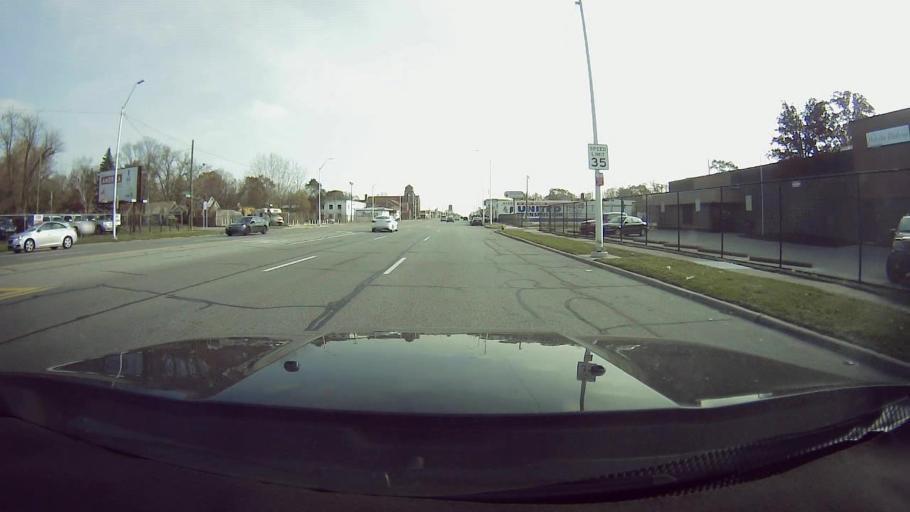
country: US
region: Michigan
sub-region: Wayne County
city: Redford
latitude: 42.4197
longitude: -83.2660
